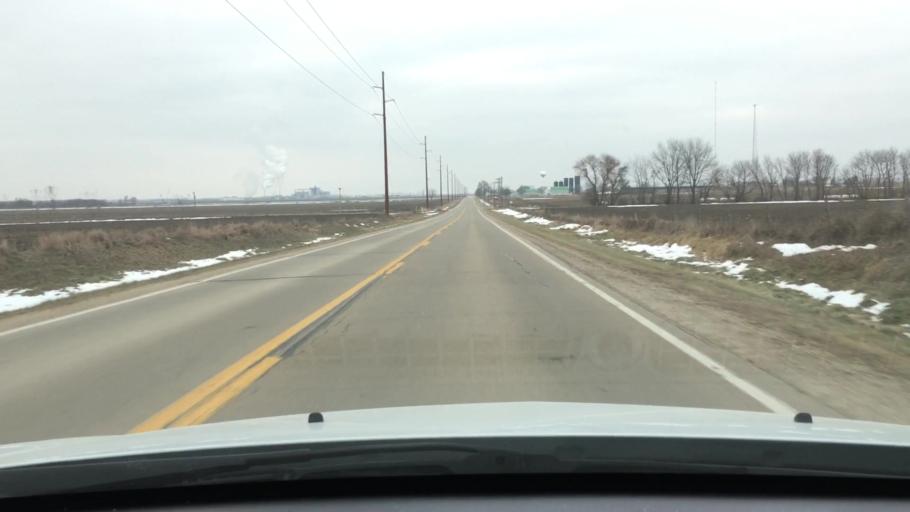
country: US
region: Illinois
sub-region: Ogle County
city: Rochelle
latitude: 41.8598
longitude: -89.0248
